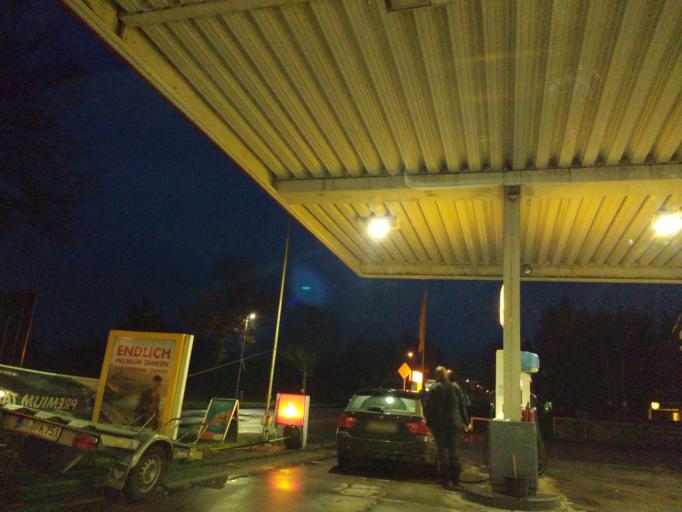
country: DE
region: Lower Saxony
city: Marxen
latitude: 53.3425
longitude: 10.0439
